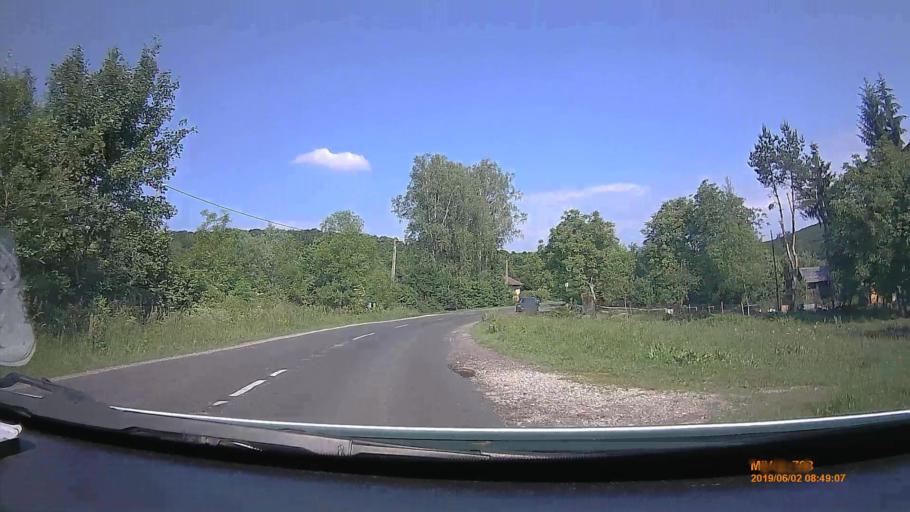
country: HU
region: Borsod-Abauj-Zemplen
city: Sajobabony
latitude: 48.1409
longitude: 20.7005
